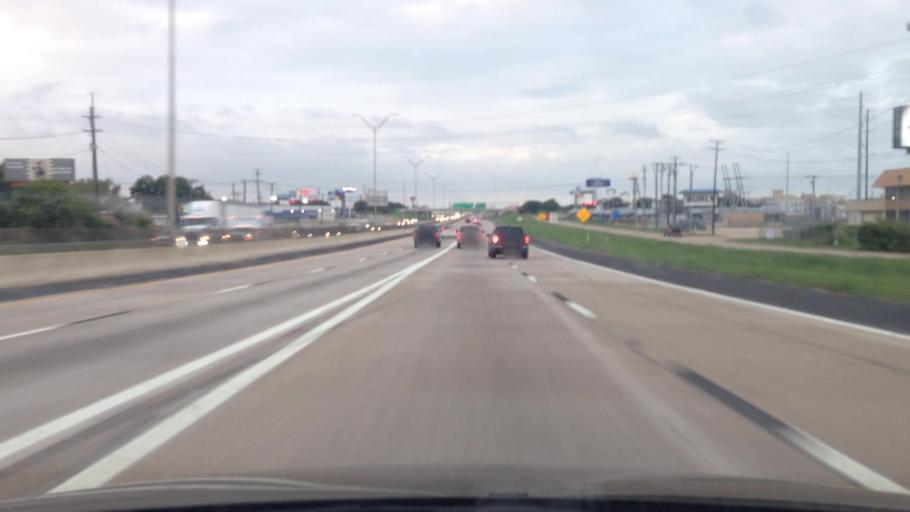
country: US
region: Texas
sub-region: Johnson County
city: Burleson
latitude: 32.5566
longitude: -97.3187
